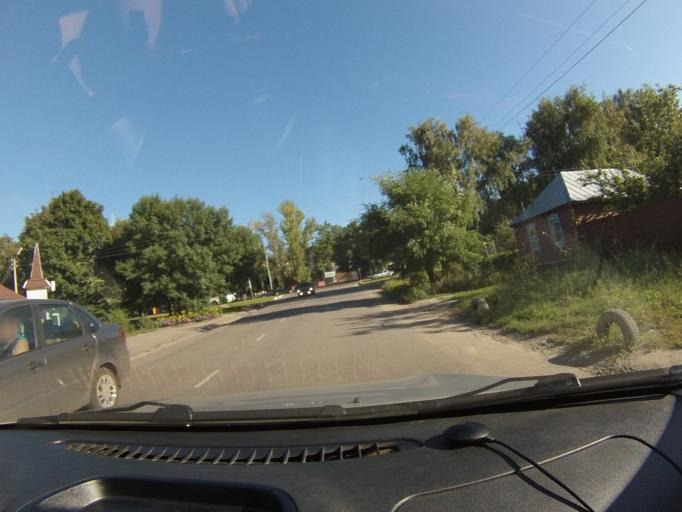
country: RU
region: Tambov
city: Tambov
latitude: 52.7548
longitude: 41.4265
